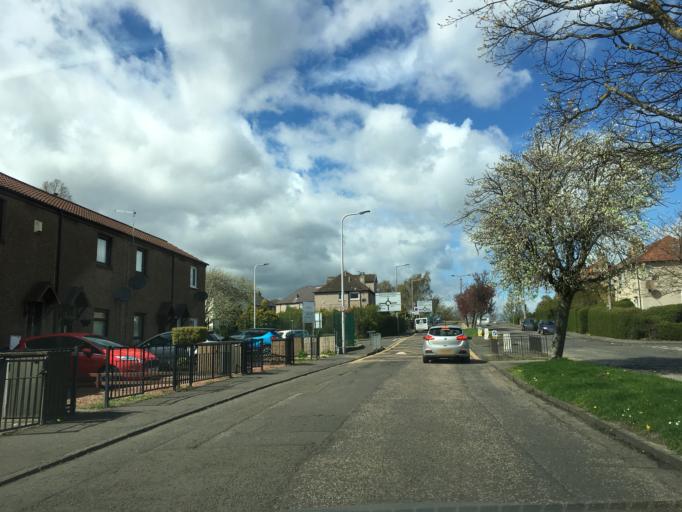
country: GB
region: Scotland
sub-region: Edinburgh
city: Colinton
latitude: 55.9225
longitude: -3.2797
